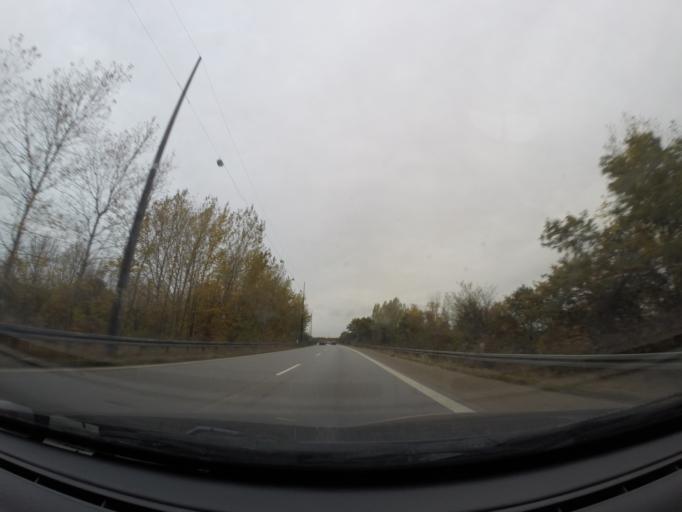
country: DK
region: Capital Region
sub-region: Ishoj Kommune
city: Ishoj
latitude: 55.6399
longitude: 12.3365
